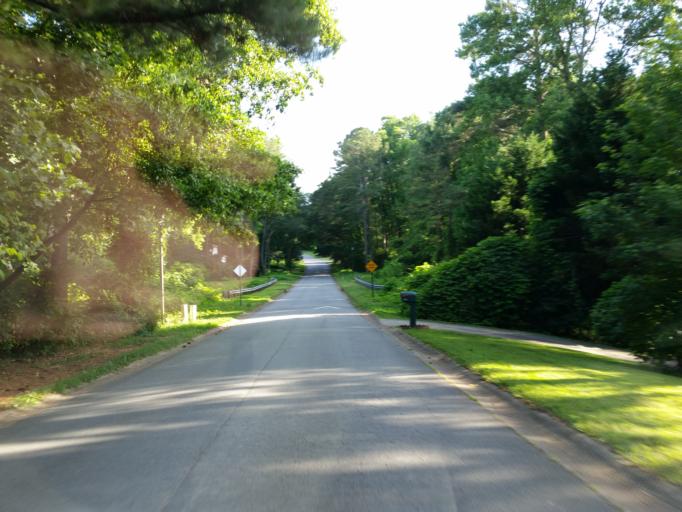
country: US
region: Georgia
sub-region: Cherokee County
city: Woodstock
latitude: 34.0648
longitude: -84.4866
